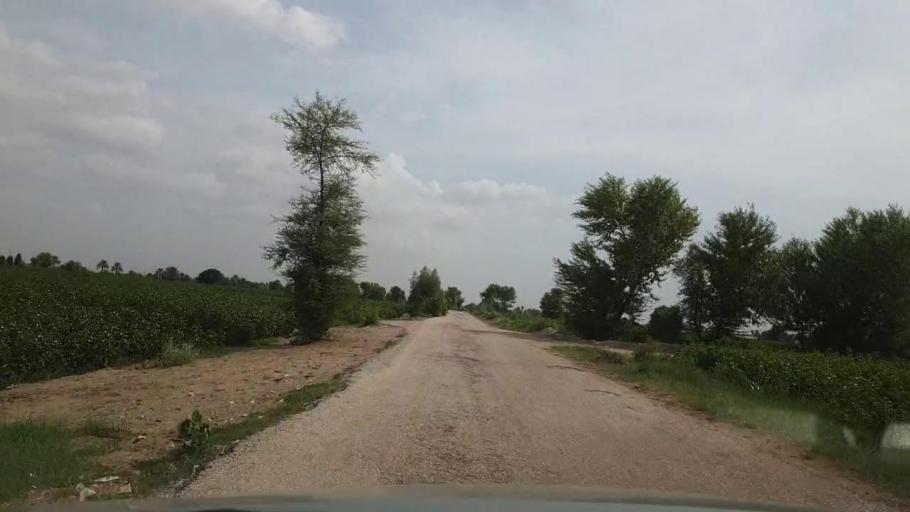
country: PK
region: Sindh
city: Kot Diji
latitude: 27.1336
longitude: 69.0280
